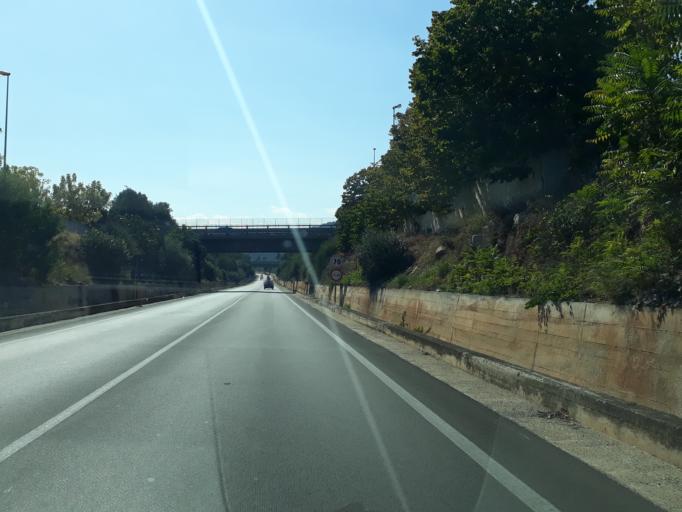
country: IT
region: Apulia
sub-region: Provincia di Brindisi
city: Fasano
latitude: 40.8423
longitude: 17.3532
